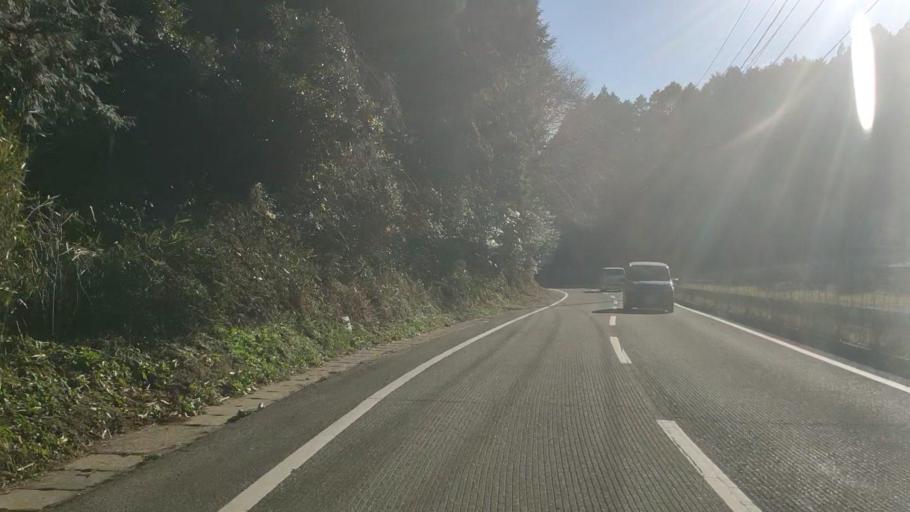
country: JP
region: Saga Prefecture
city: Kanzakimachi-kanzaki
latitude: 33.3970
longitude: 130.2717
